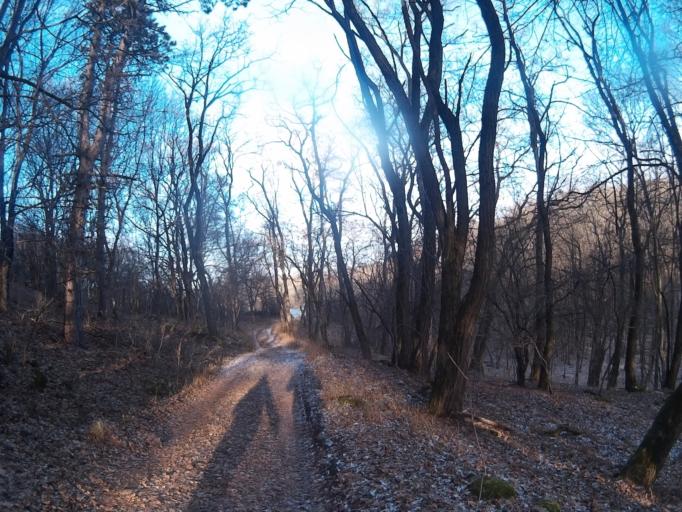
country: HU
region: Borsod-Abauj-Zemplen
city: Rudabanya
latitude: 48.5386
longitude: 20.6378
